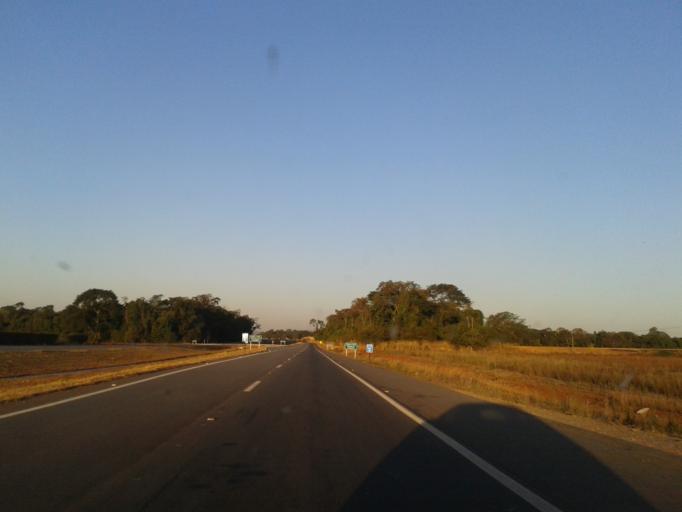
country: BR
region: Goias
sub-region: Itaberai
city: Itaberai
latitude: -16.0157
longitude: -49.8885
